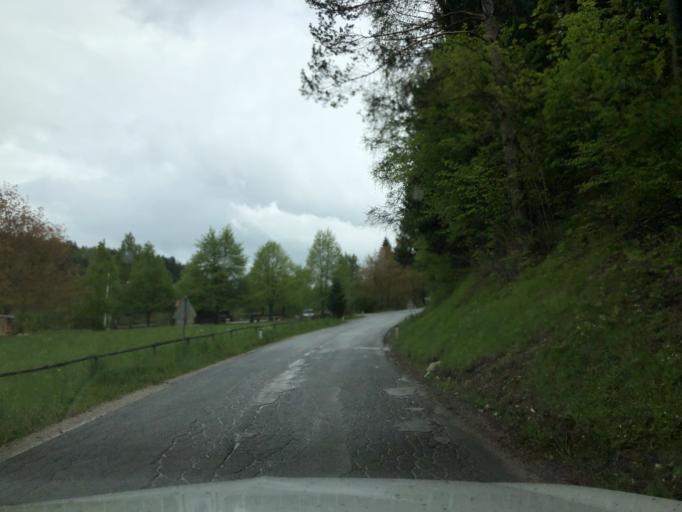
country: SI
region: Gorje
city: Zgornje Gorje
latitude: 46.3927
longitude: 14.0730
